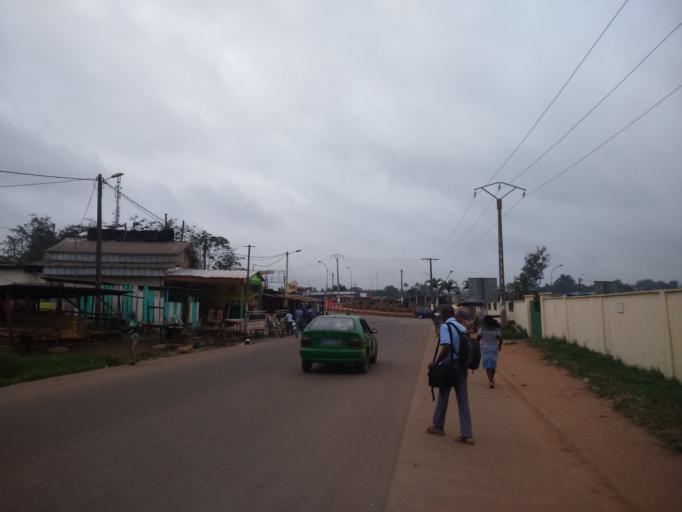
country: CI
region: Agneby
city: Agboville
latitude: 5.9320
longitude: -4.2140
